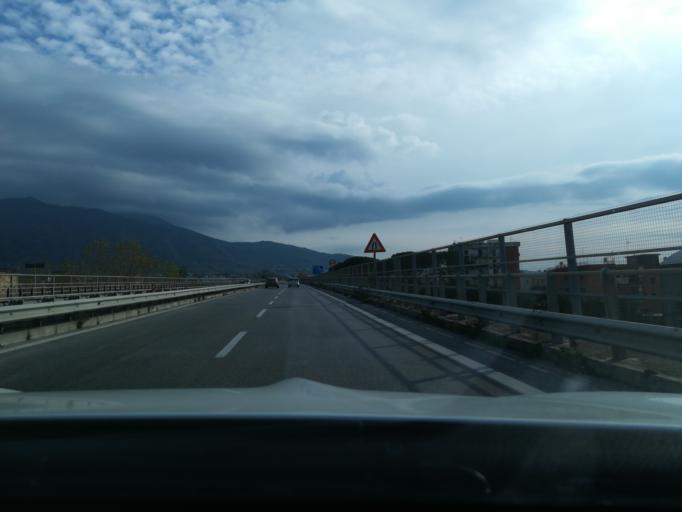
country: IT
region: Campania
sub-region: Provincia di Napoli
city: Cercola
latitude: 40.8639
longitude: 14.3640
